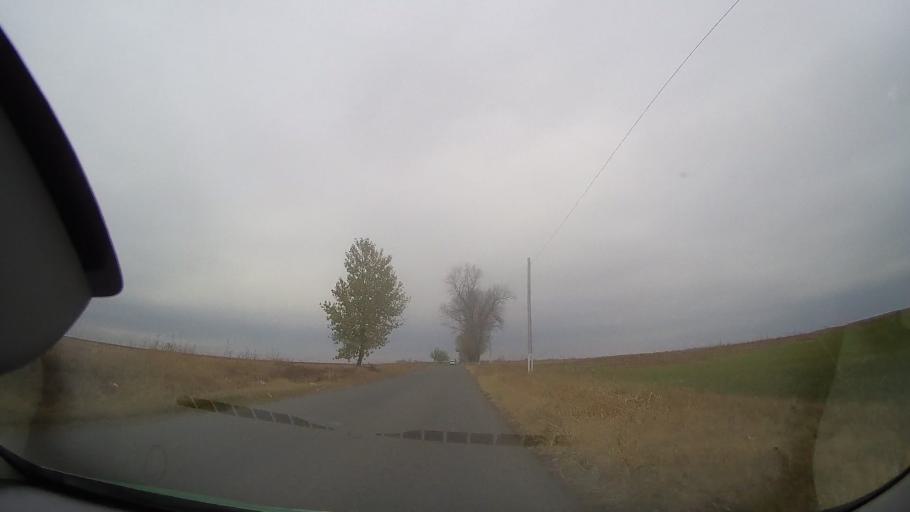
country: RO
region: Braila
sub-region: Comuna Budesti
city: Tataru
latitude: 44.8643
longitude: 27.4262
